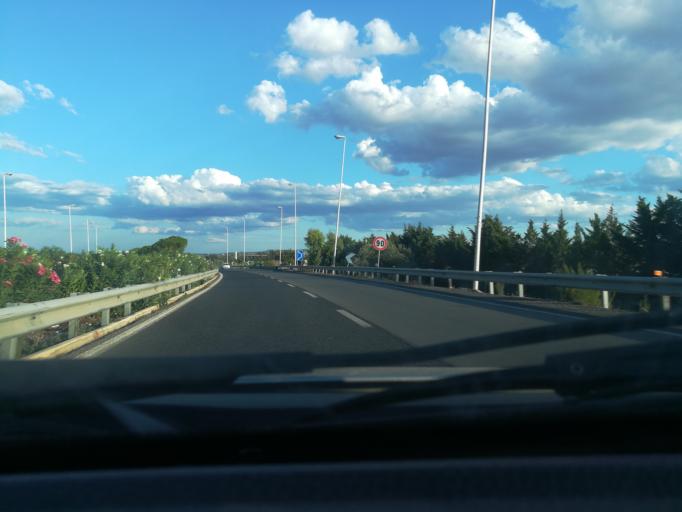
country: IT
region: Apulia
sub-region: Provincia di Bari
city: Mola di Bari
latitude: 41.0497
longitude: 17.0754
